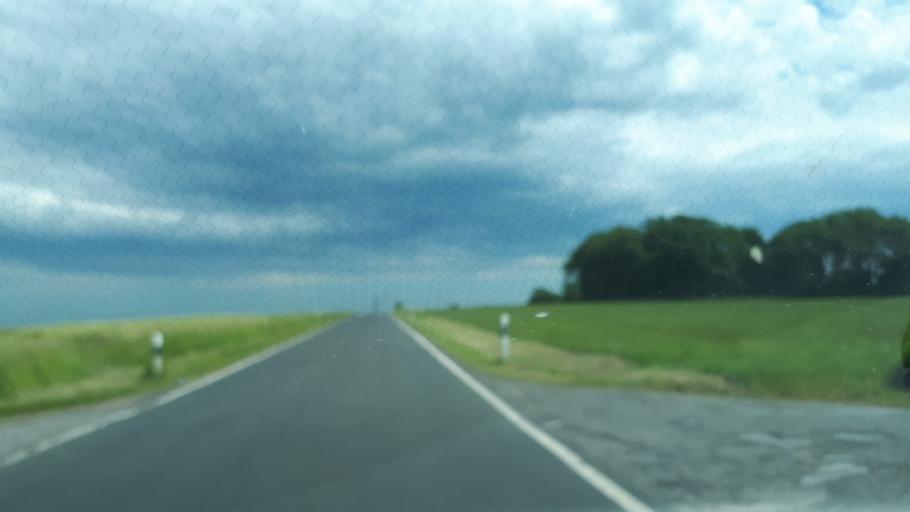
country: DE
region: Rheinland-Pfalz
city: Immerath
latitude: 50.1358
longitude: 6.9500
